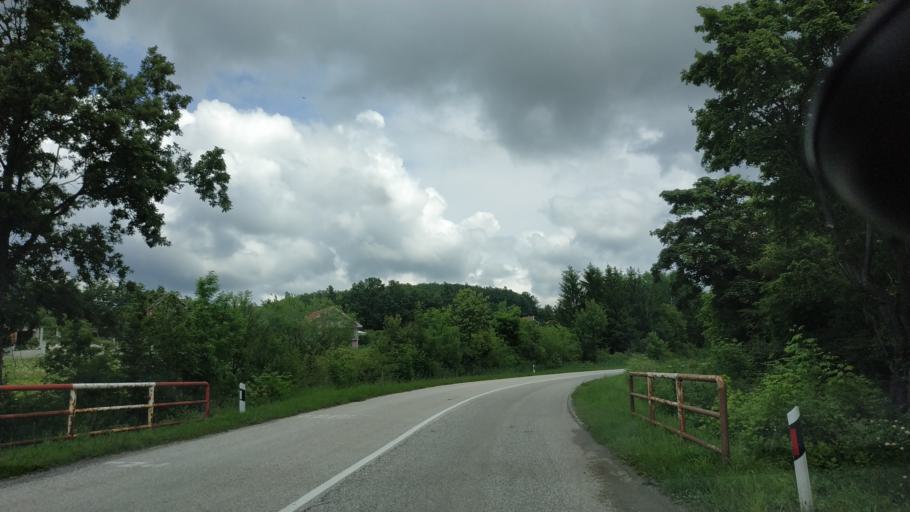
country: RS
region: Central Serbia
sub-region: Borski Okrug
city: Bor
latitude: 44.0899
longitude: 21.9995
